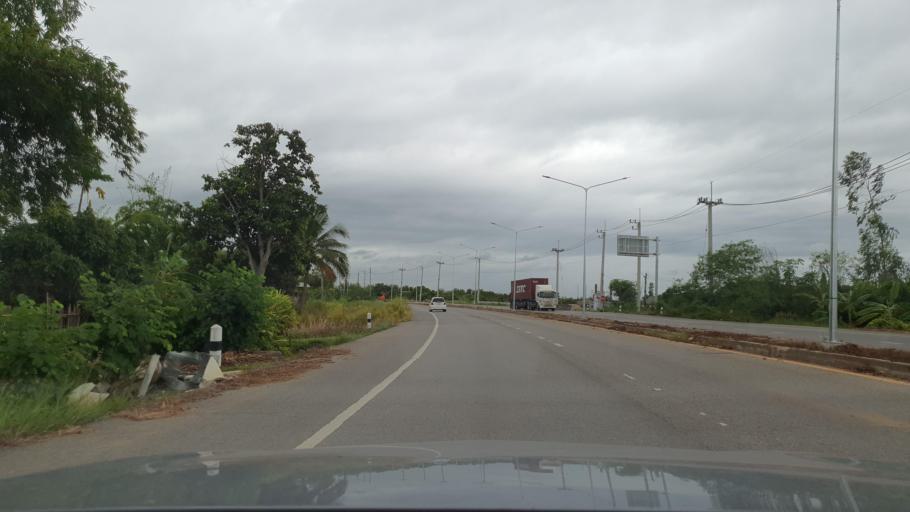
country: TH
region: Lamphun
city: Lamphun
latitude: 18.6128
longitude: 99.0177
